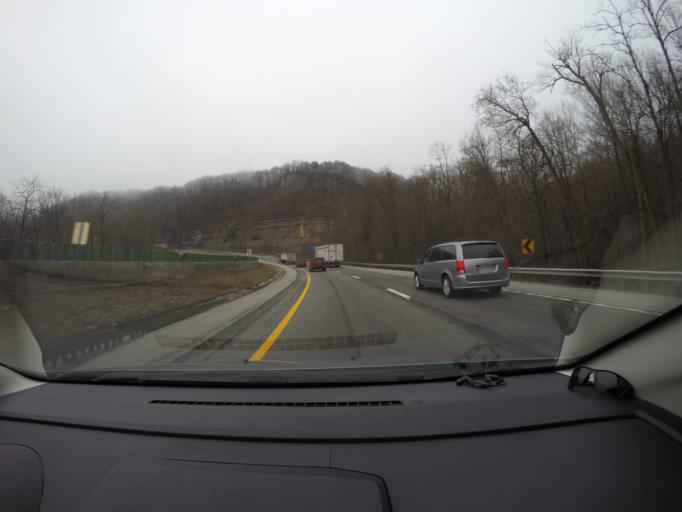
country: US
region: Tennessee
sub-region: Marion County
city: Monteagle
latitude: 35.2394
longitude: -85.8763
